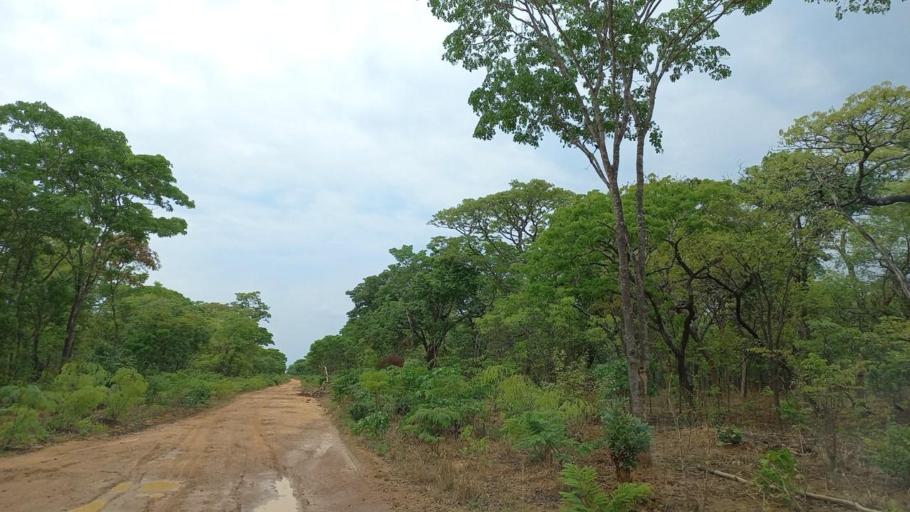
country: ZM
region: North-Western
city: Kalengwa
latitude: -13.5880
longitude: 24.9722
